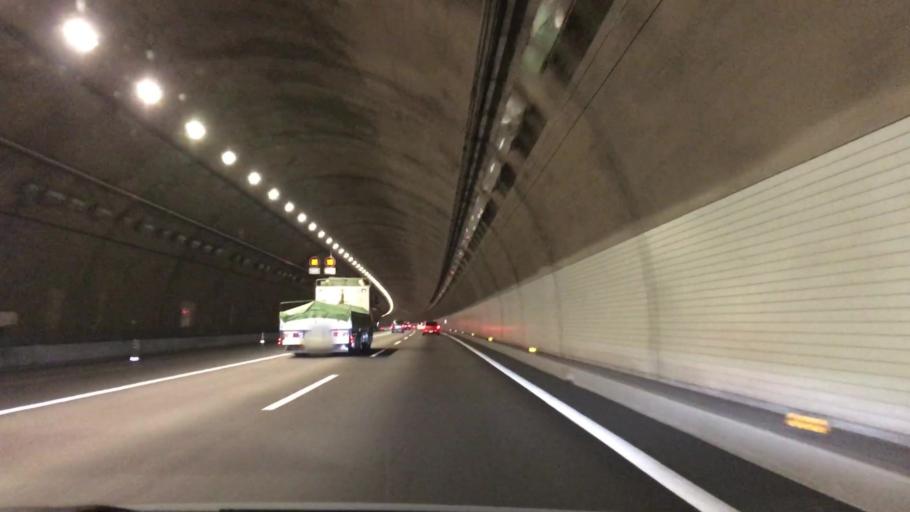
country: JP
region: Shizuoka
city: Shizuoka-shi
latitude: 35.0131
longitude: 138.3261
